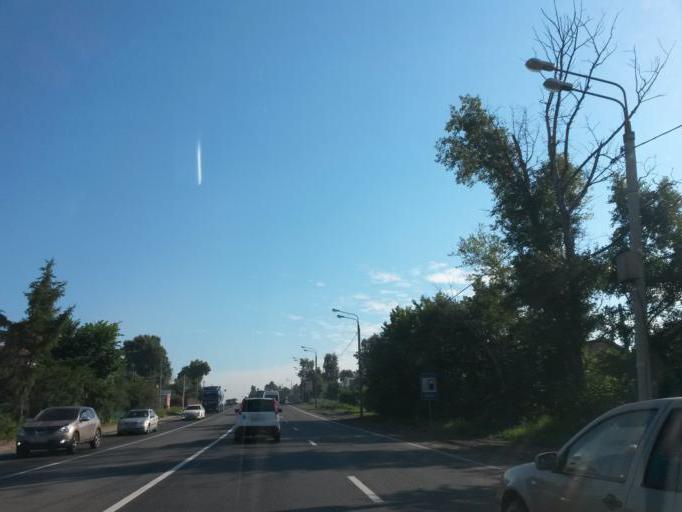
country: RU
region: Moskovskaya
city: Yam
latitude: 55.5059
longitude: 37.7530
